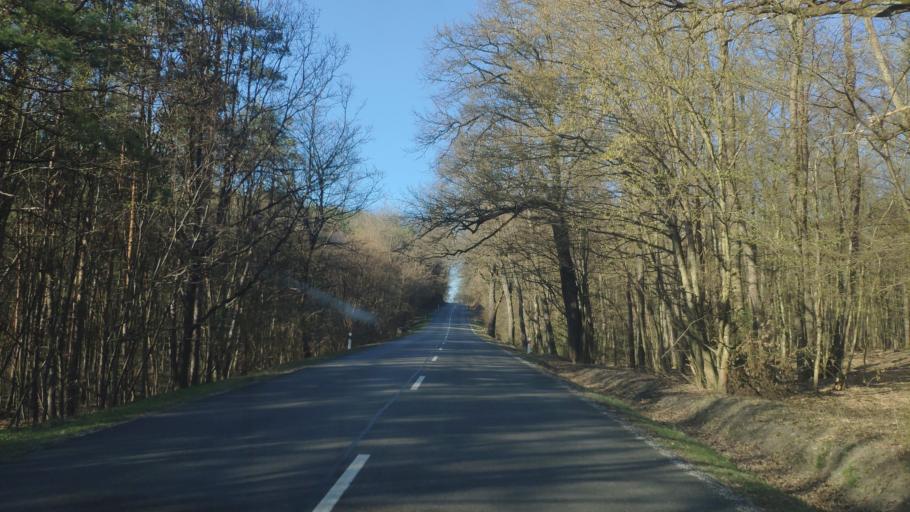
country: SK
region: Banskobystricky
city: Revuca
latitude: 48.5016
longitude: 20.2865
